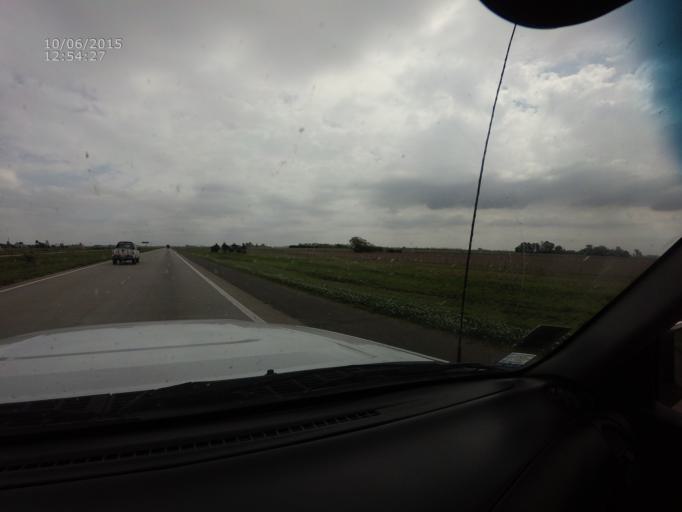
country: AR
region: Santa Fe
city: Armstrong
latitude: -32.8152
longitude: -61.5728
